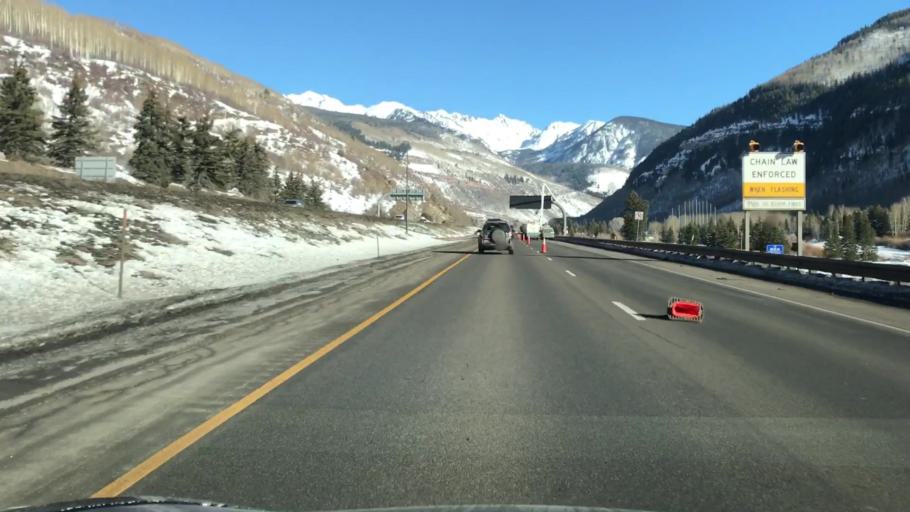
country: US
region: Colorado
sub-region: Eagle County
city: Vail
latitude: 39.6419
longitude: -106.3551
